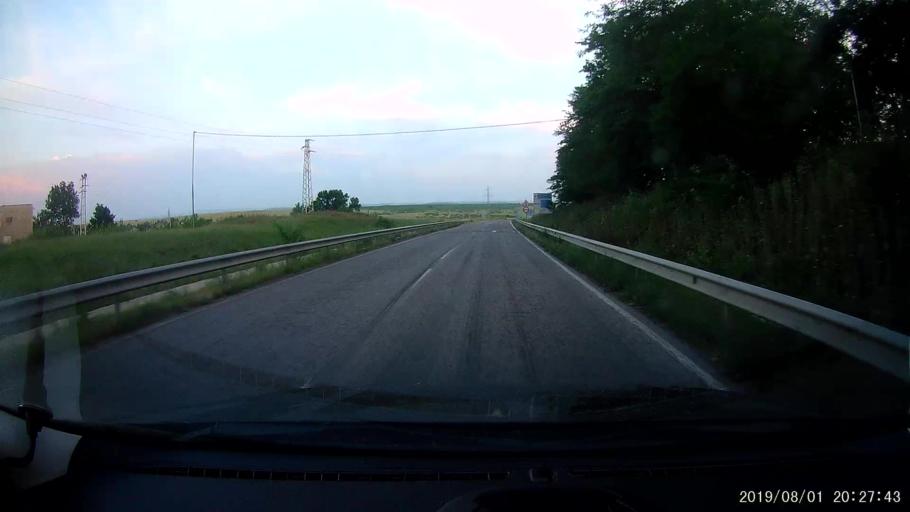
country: BG
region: Yambol
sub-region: Obshtina Elkhovo
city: Elkhovo
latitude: 42.1754
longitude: 26.5837
